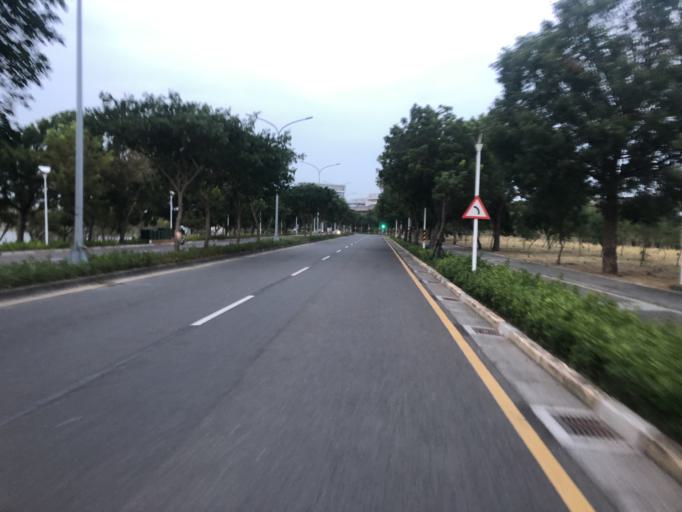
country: TW
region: Taiwan
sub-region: Tainan
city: Tainan
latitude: 23.0852
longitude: 120.2850
